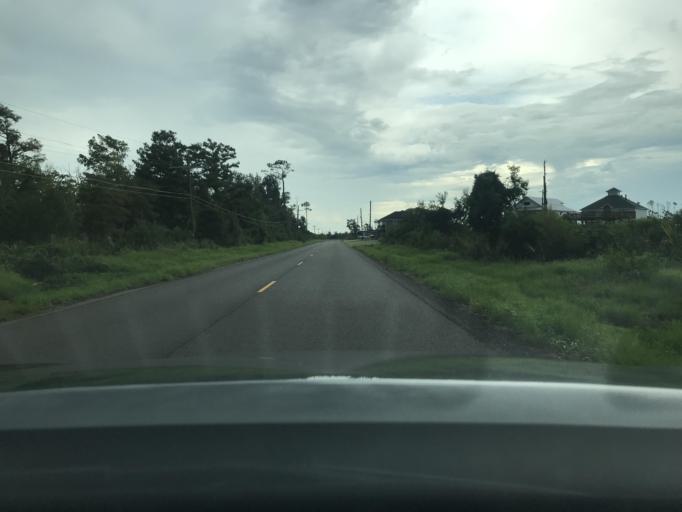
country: US
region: Louisiana
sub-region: Calcasieu Parish
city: Westlake
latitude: 30.2570
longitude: -93.2270
